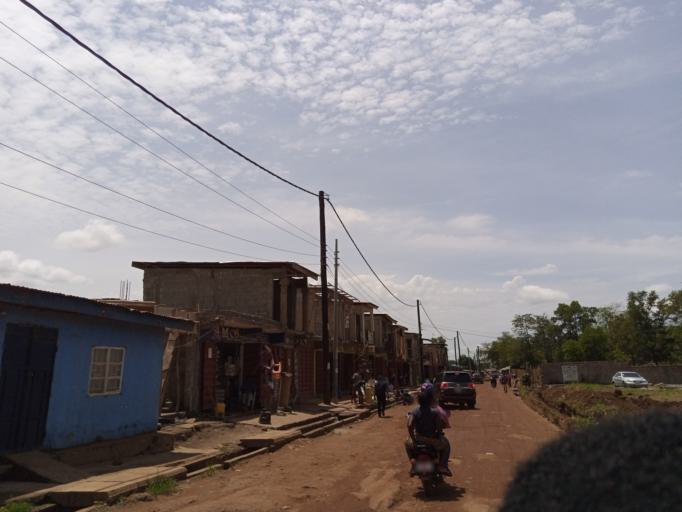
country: SL
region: Western Area
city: Hastings
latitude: 8.3817
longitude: -13.1358
